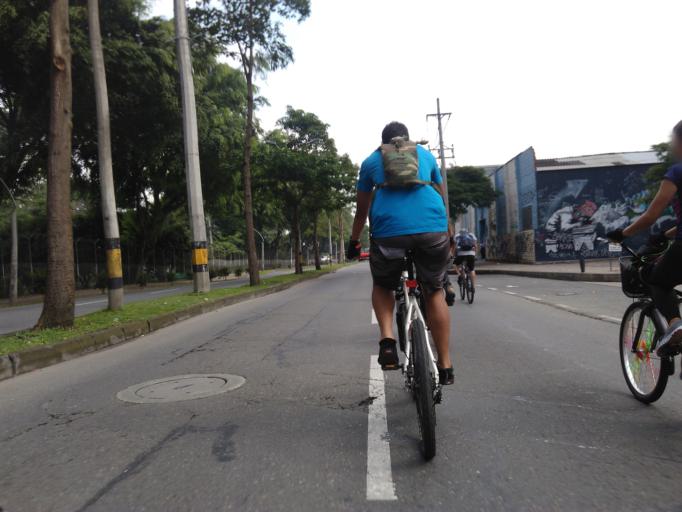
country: CO
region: Antioquia
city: Medellin
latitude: 6.2654
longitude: -75.5672
